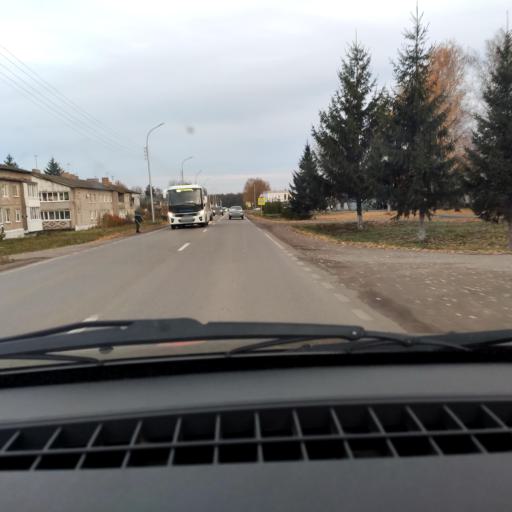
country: RU
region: Bashkortostan
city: Mikhaylovka
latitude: 54.8122
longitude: 55.8060
